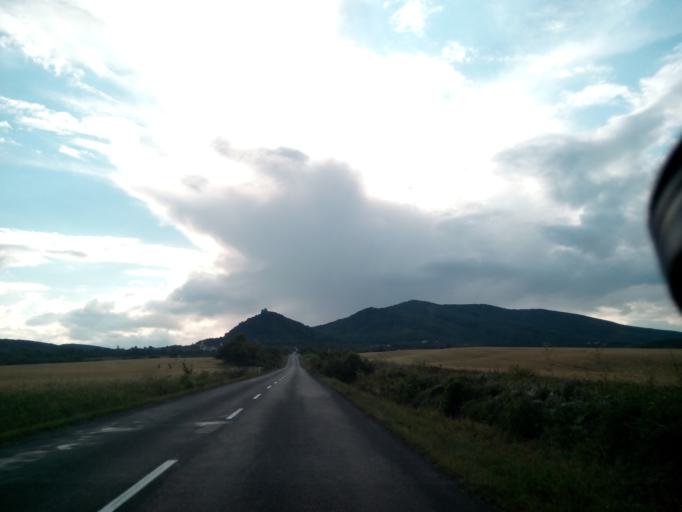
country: SK
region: Kosicky
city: Secovce
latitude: 48.6352
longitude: 21.4998
